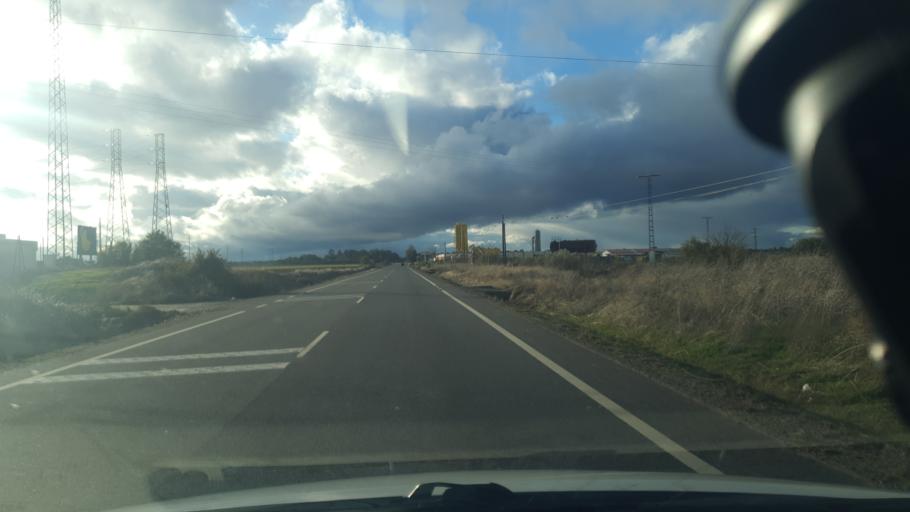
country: ES
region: Castille and Leon
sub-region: Provincia de Segovia
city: Nava de la Asuncion
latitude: 41.1559
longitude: -4.4988
